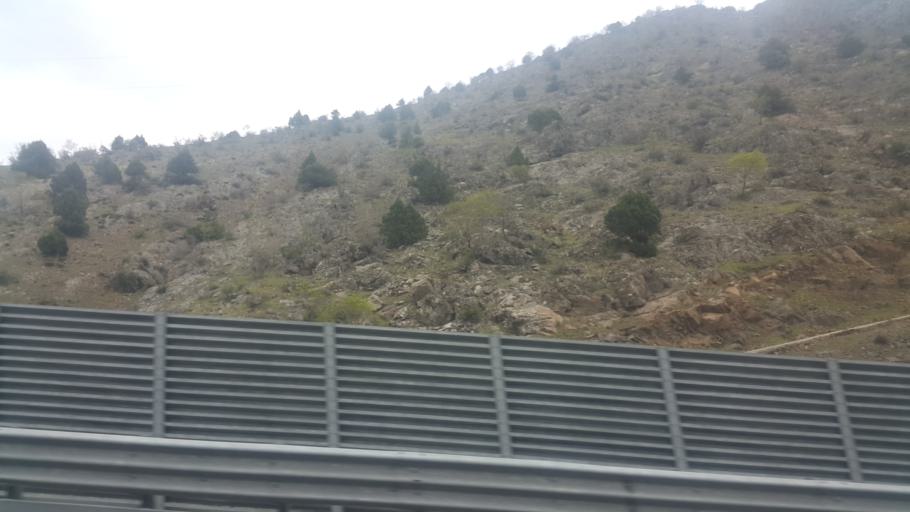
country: TR
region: Nigde
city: Ciftehan
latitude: 37.5672
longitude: 34.7555
